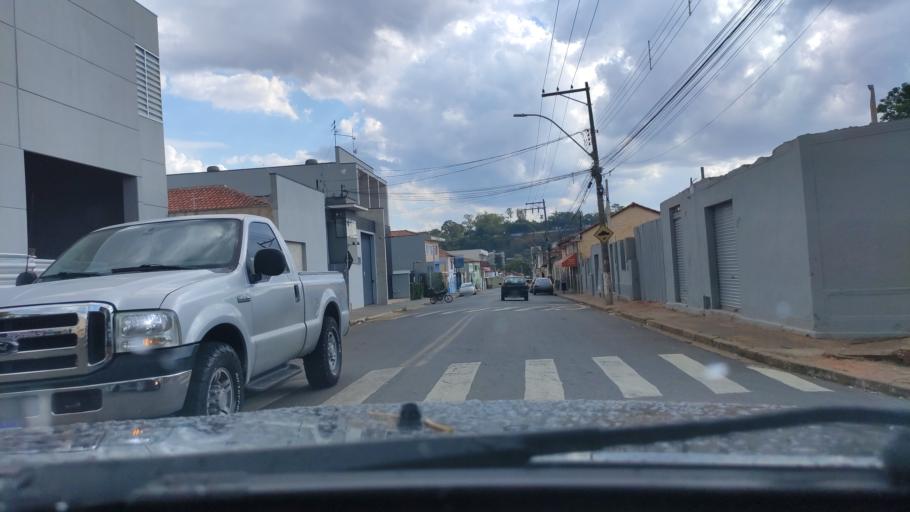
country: BR
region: Sao Paulo
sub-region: Itapira
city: Itapira
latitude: -22.4385
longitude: -46.8137
